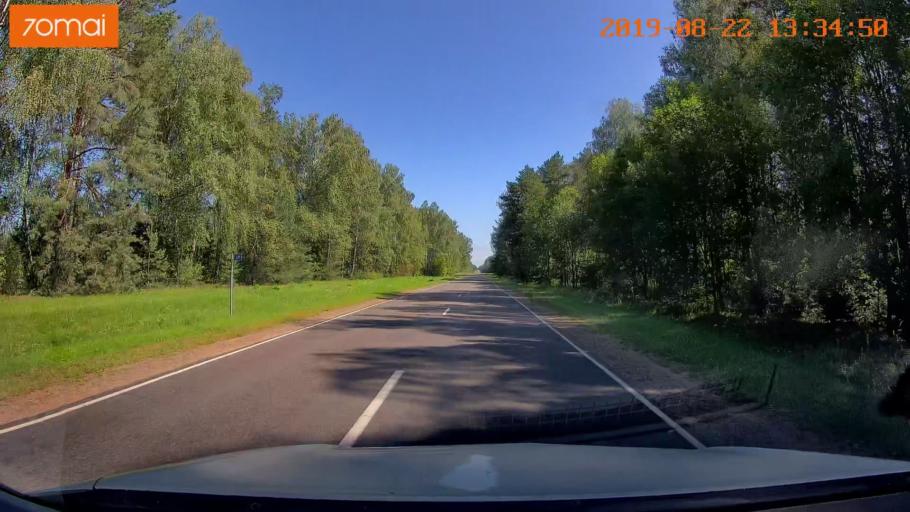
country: BY
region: Minsk
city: Staryya Darohi
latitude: 53.2146
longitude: 28.2518
